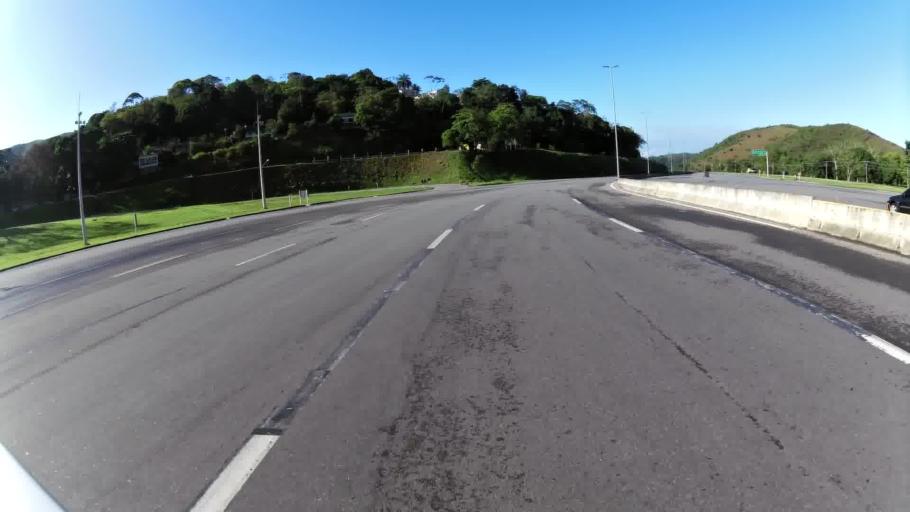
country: BR
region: Rio de Janeiro
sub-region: Petropolis
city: Petropolis
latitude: -22.6108
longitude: -43.2856
